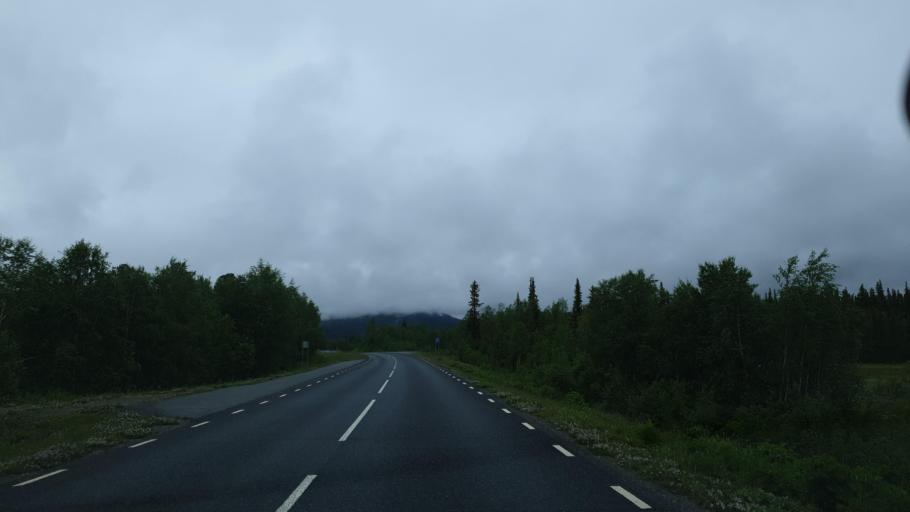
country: SE
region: Vaesterbotten
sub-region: Vilhelmina Kommun
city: Sjoberg
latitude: 65.2500
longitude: 15.7335
